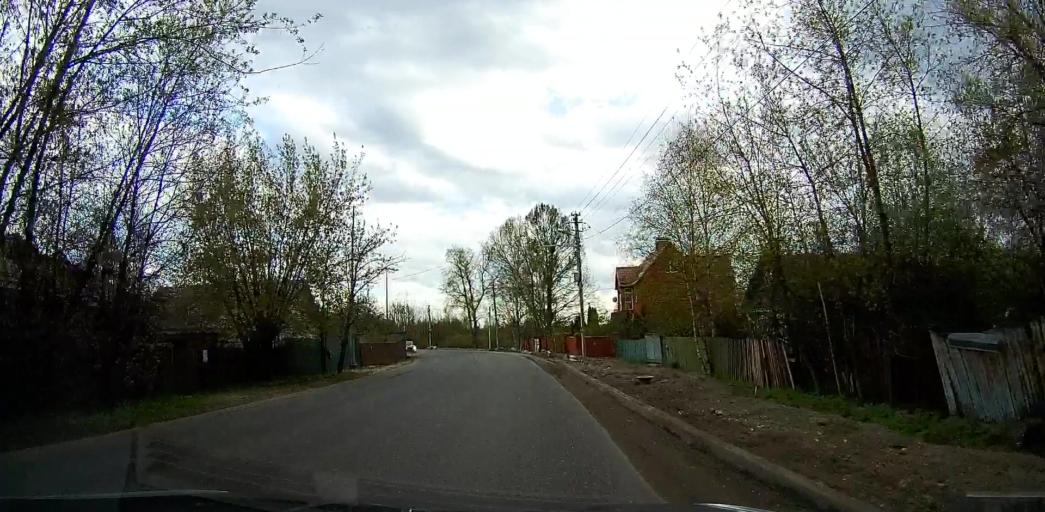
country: RU
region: Moskovskaya
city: Pavlovskiy Posad
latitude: 55.8003
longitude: 38.6861
